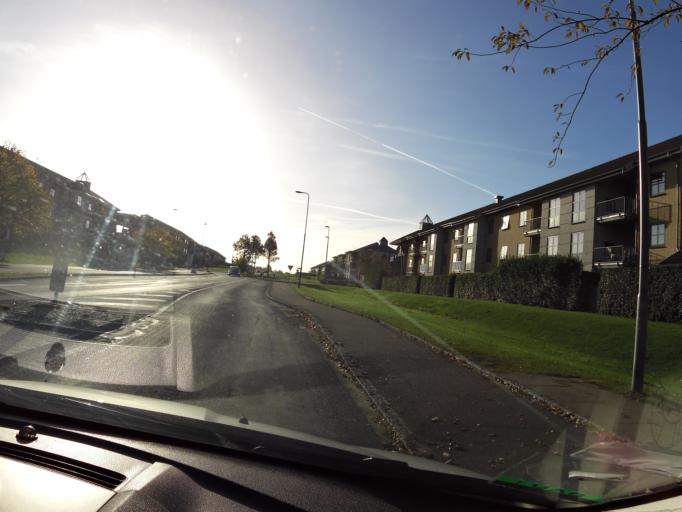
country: DK
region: South Denmark
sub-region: Odense Kommune
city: Hojby
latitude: 55.3279
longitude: 10.4391
